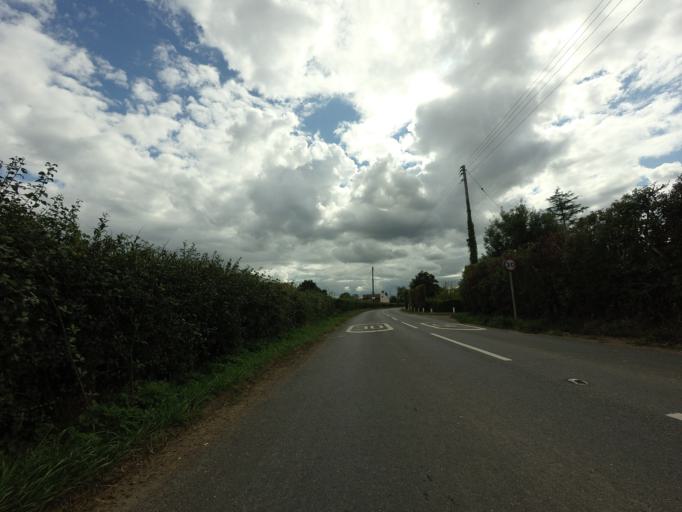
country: GB
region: England
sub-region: Kent
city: Marden
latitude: 51.1861
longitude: 0.4555
